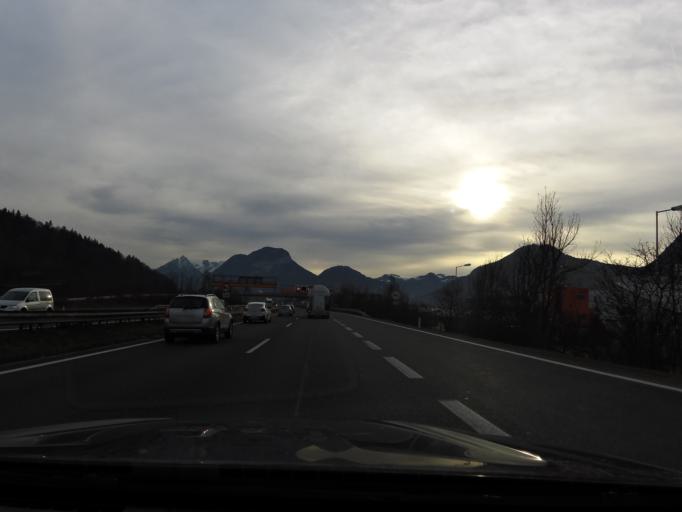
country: AT
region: Tyrol
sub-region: Politischer Bezirk Kufstein
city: Worgl
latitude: 47.4844
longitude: 12.0326
